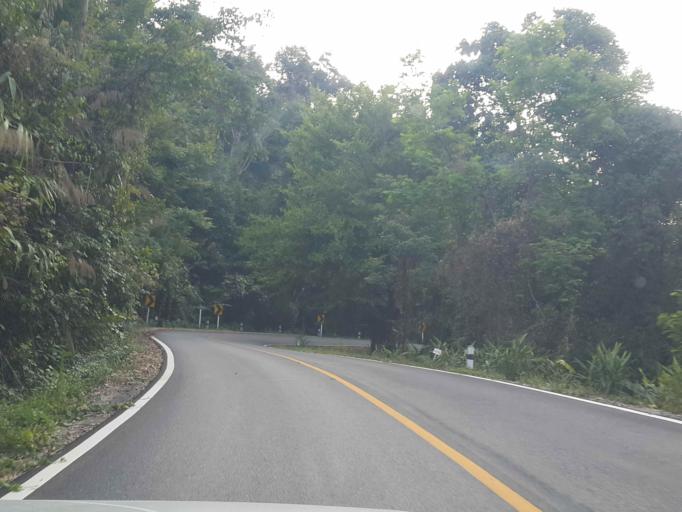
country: TH
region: Chiang Mai
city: Mae On
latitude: 18.9592
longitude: 99.3329
